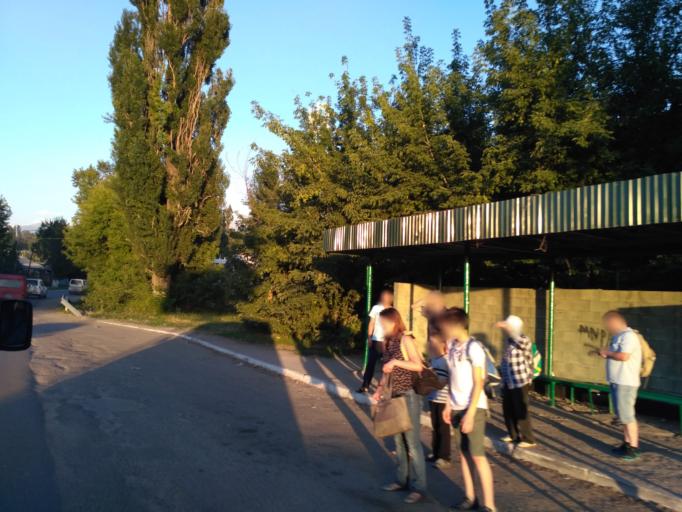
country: KZ
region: Almaty Qalasy
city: Almaty
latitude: 43.1775
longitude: 76.7561
